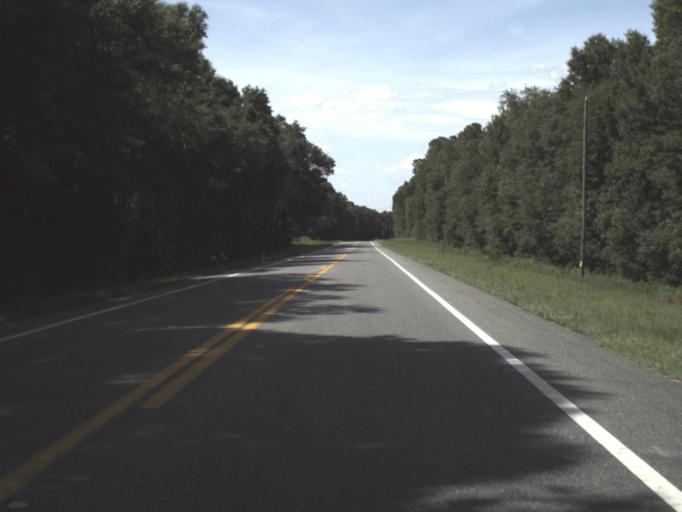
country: US
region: Florida
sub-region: Alachua County
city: High Springs
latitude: 29.8543
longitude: -82.7420
